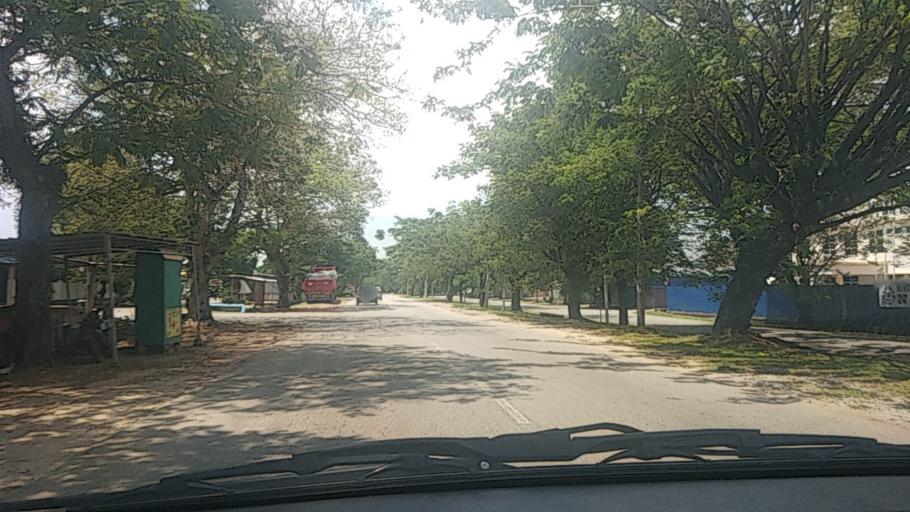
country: MY
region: Kedah
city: Sungai Petani
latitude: 5.6459
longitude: 100.5227
